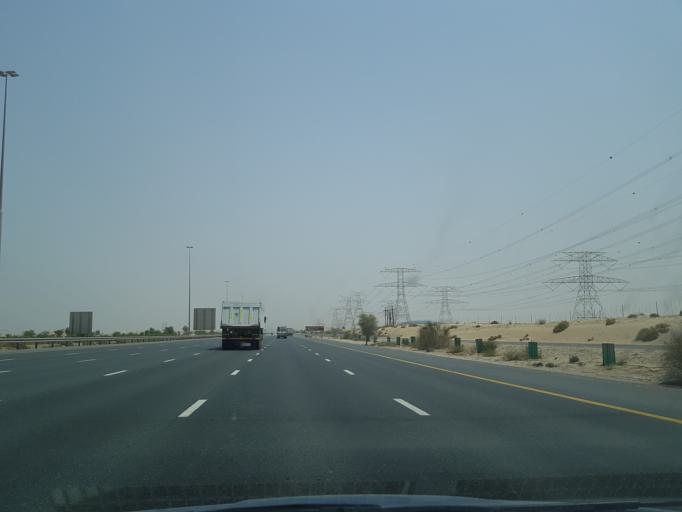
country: AE
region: Dubai
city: Dubai
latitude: 25.0409
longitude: 55.3010
